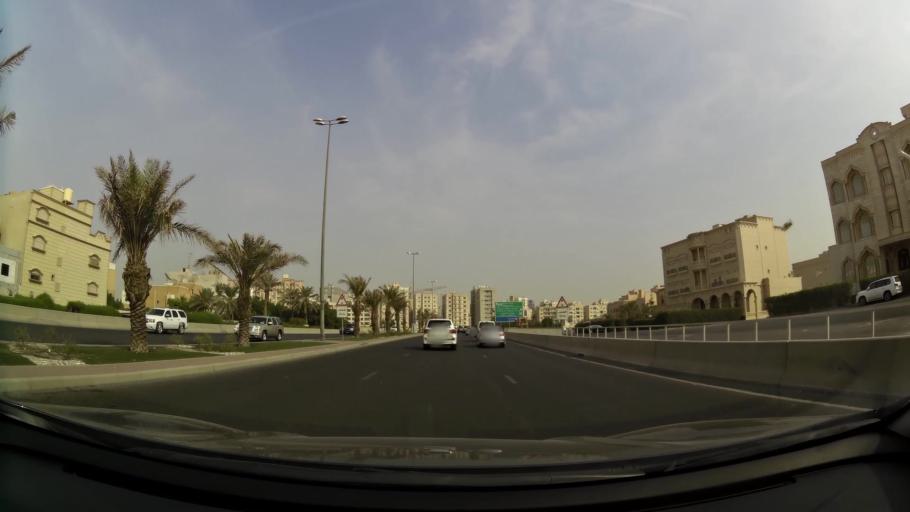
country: KW
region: Al Farwaniyah
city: Al Farwaniyah
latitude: 29.2798
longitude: 47.9465
